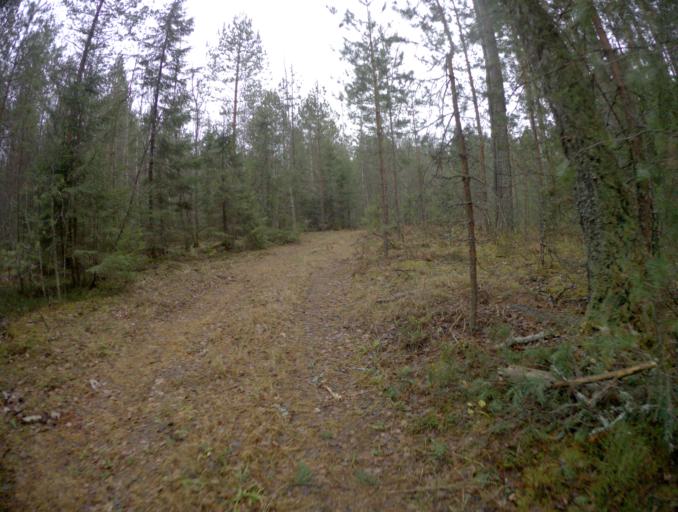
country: RU
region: Vladimir
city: Golovino
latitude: 56.0171
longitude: 40.5323
